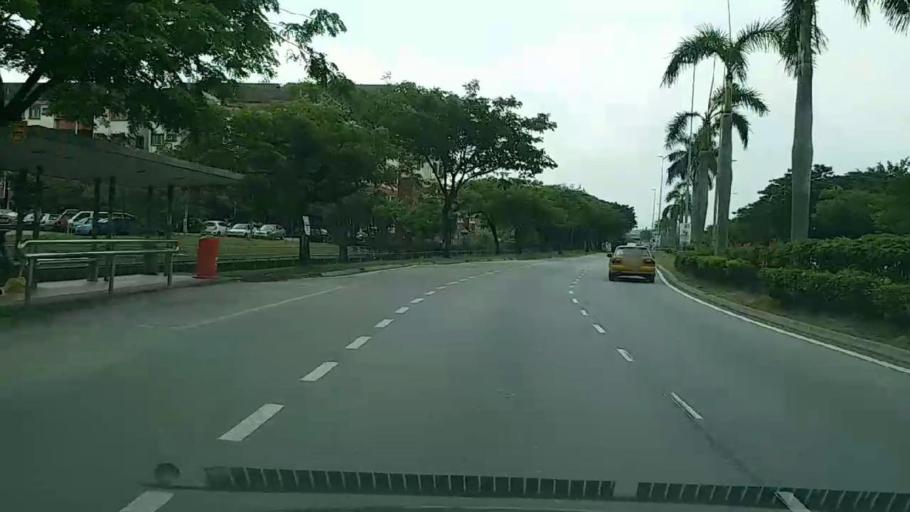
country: MY
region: Putrajaya
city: Putrajaya
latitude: 2.9451
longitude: 101.6169
